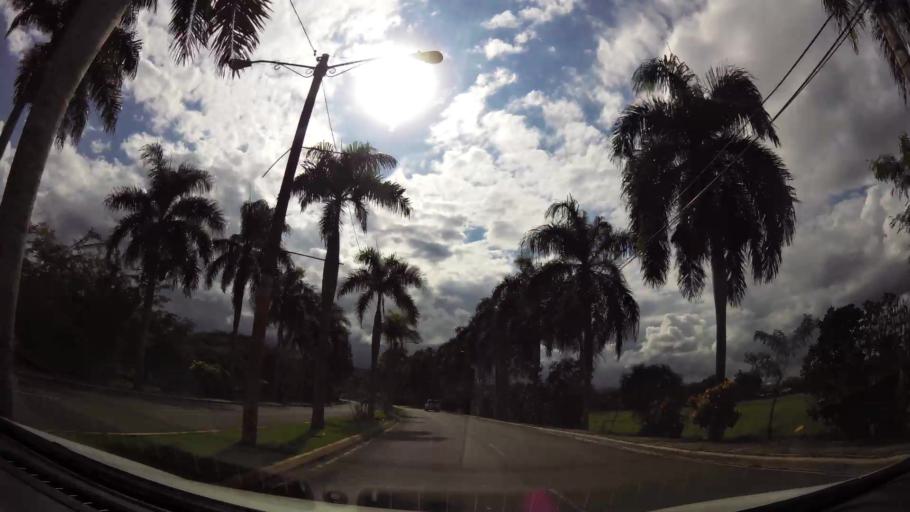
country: DO
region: La Vega
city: Concepcion de La Vega
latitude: 19.2016
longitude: -70.4987
